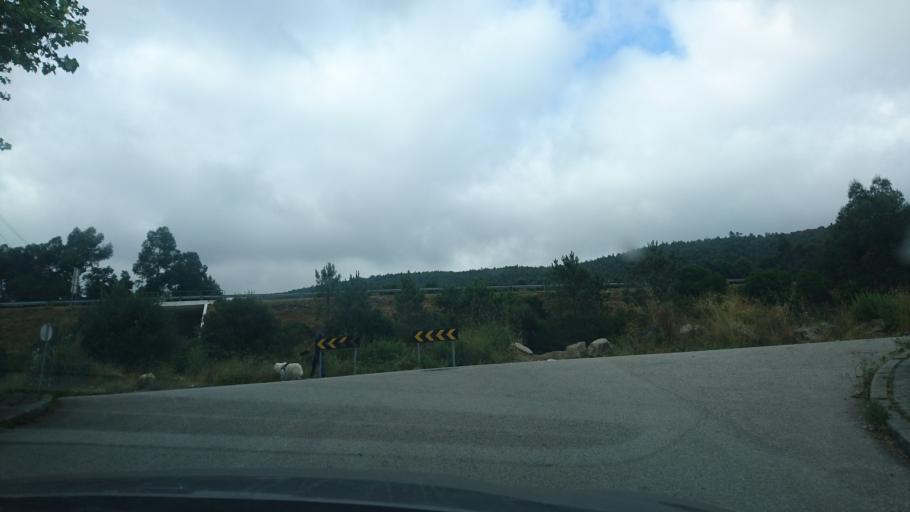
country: PT
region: Porto
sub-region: Valongo
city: Valongo
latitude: 41.1956
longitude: -8.4890
